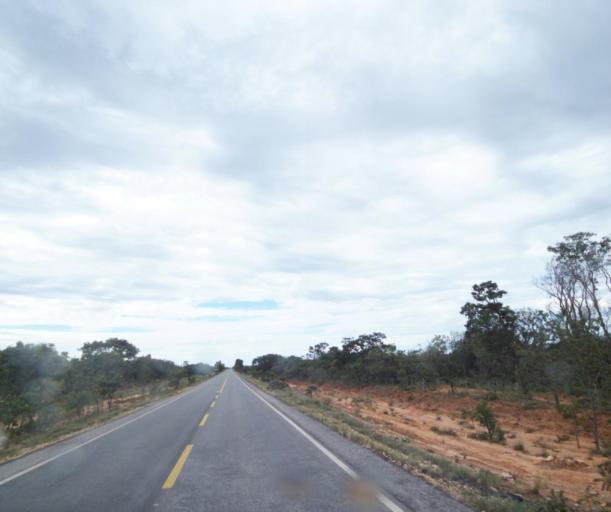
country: BR
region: Bahia
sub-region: Sao Felix Do Coribe
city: Santa Maria da Vitoria
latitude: -13.9753
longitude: -44.4463
